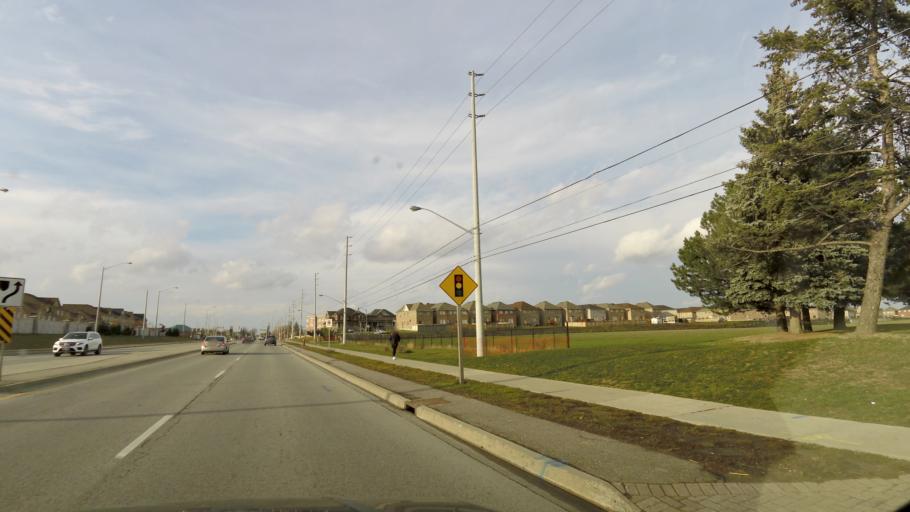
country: CA
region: Ontario
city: Brampton
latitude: 43.7813
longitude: -79.6753
